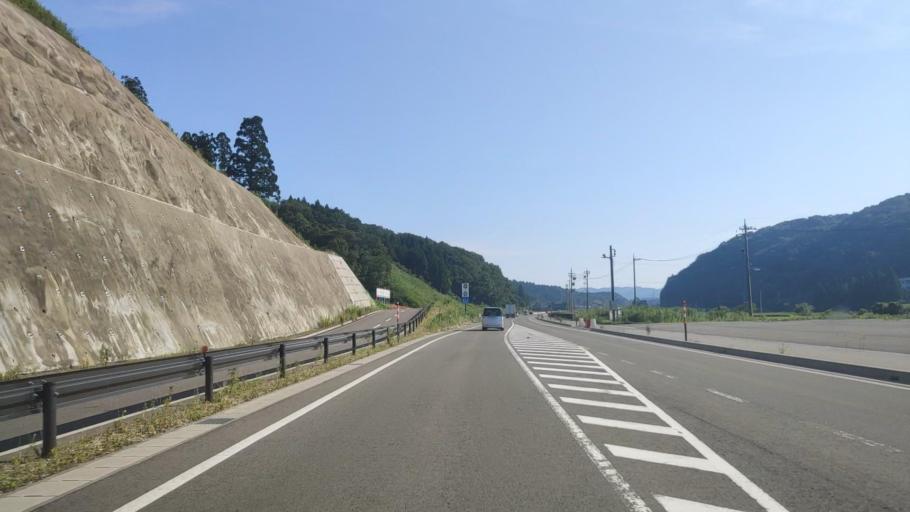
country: JP
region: Fukui
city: Maruoka
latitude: 36.2075
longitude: 136.2684
